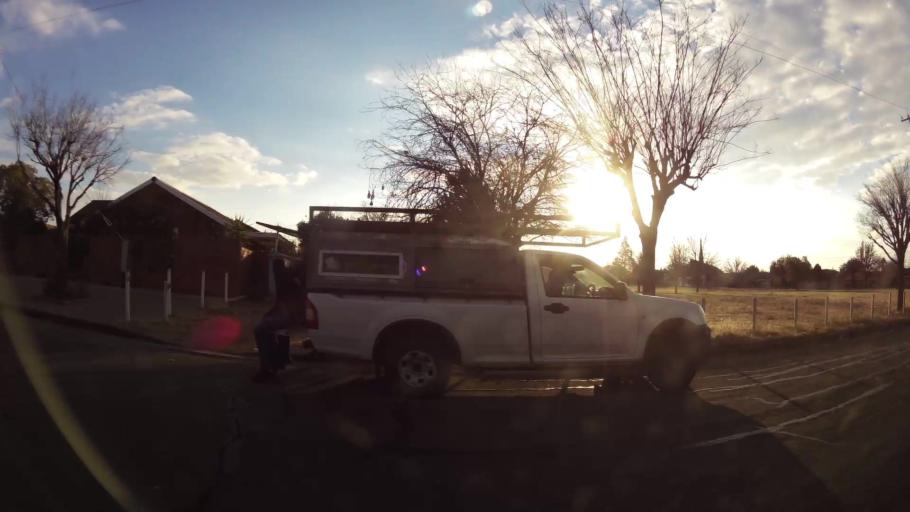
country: ZA
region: Orange Free State
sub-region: Mangaung Metropolitan Municipality
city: Bloemfontein
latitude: -29.1402
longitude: 26.1928
